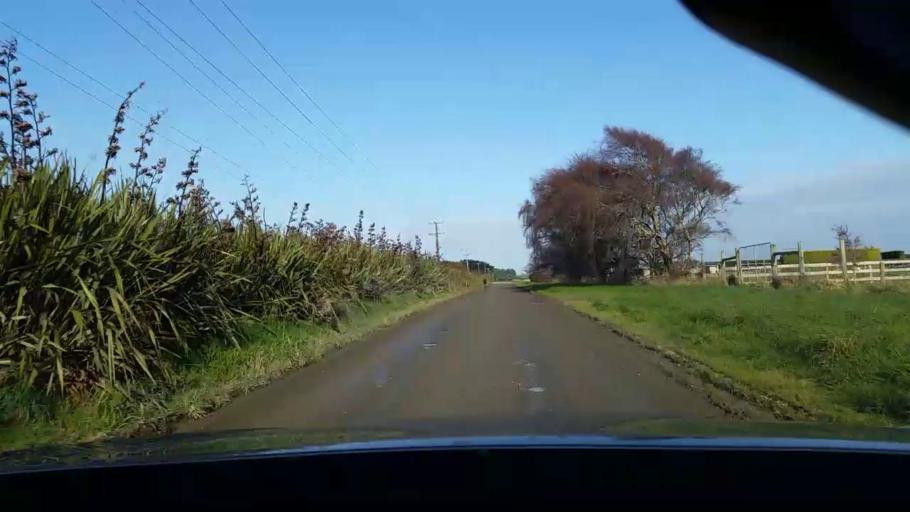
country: NZ
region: Southland
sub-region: Invercargill City
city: Invercargill
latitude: -46.3027
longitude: 168.3033
